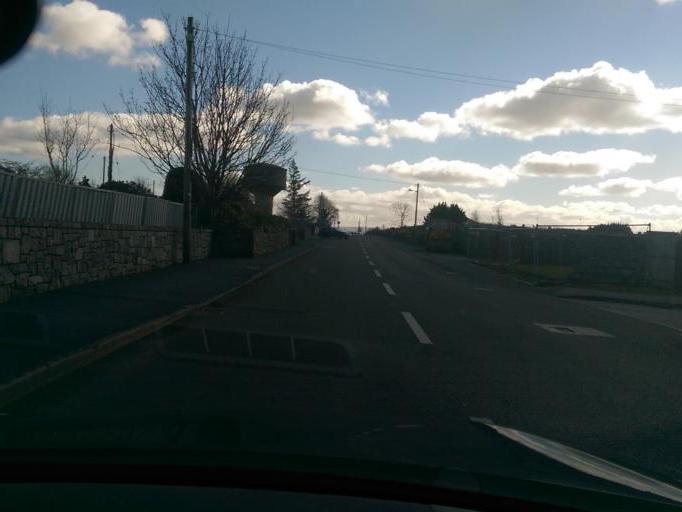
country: IE
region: Connaught
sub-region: County Galway
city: Athenry
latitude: 53.3071
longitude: -8.7523
